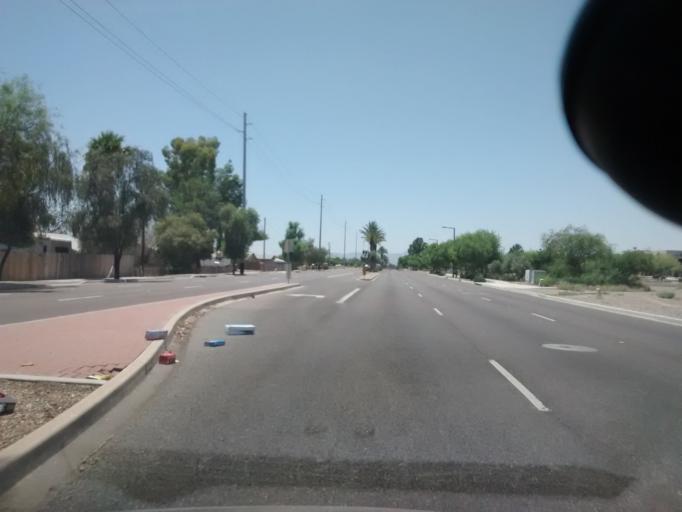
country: US
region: Arizona
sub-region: Maricopa County
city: Peoria
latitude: 33.5377
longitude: -112.2415
